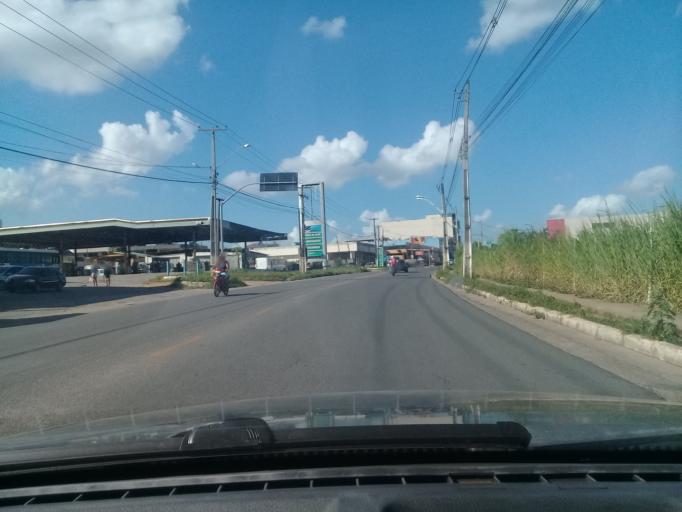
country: BR
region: Pernambuco
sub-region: Vitoria De Santo Antao
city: Vitoria de Santo Antao
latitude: -8.1148
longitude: -35.2955
